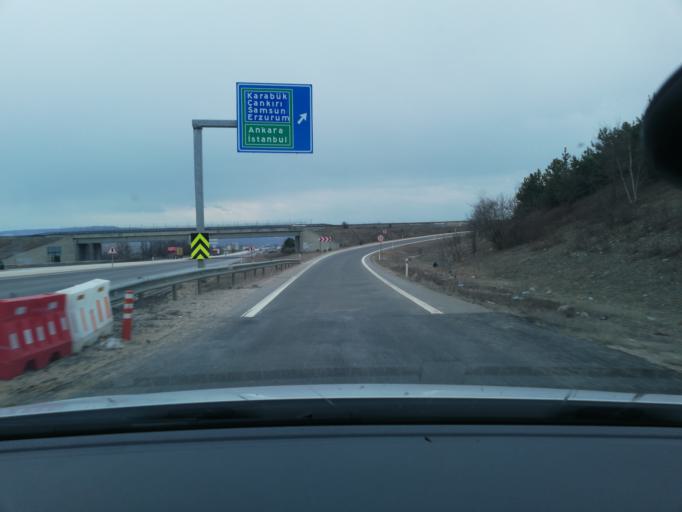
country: TR
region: Bolu
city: Gerede
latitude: 40.7778
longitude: 32.2170
